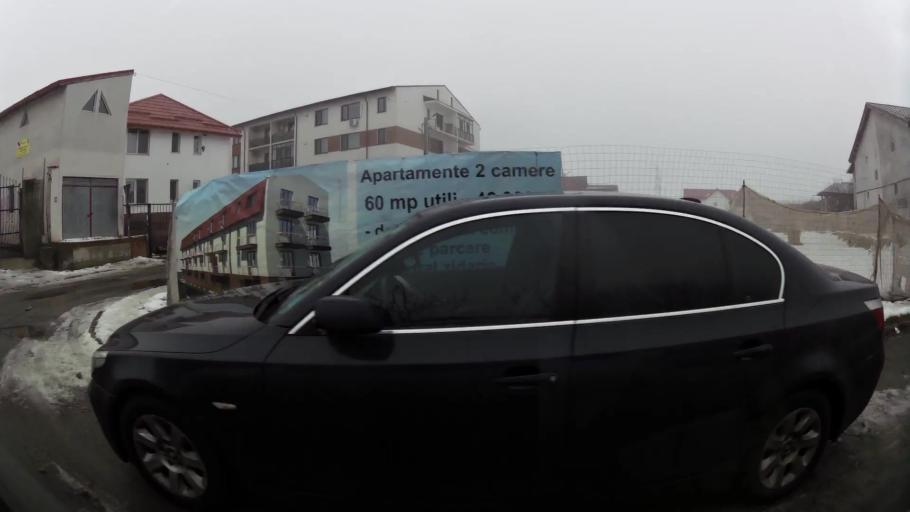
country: RO
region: Ilfov
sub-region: Comuna Chiajna
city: Rosu
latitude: 44.4429
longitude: 26.0093
